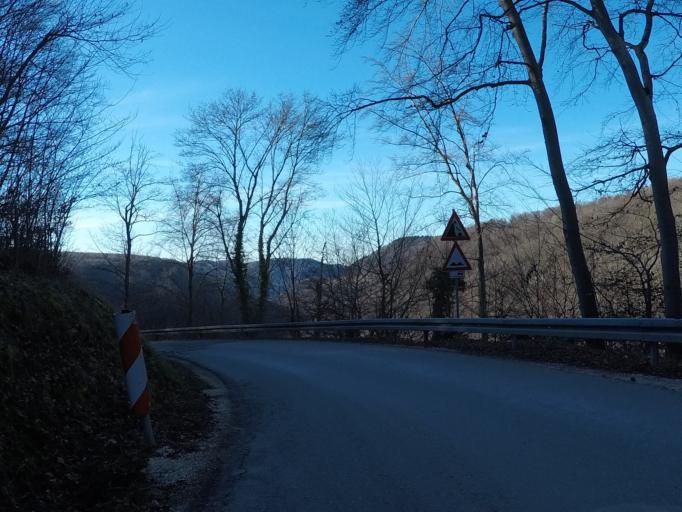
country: DE
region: Baden-Wuerttemberg
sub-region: Tuebingen Region
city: Sankt Johann
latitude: 48.4490
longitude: 9.2999
